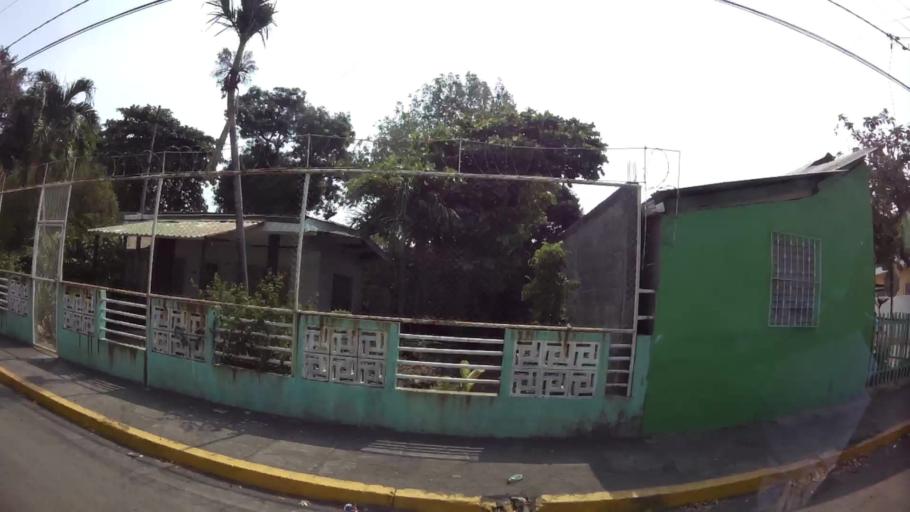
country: NI
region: Managua
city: Ciudad Sandino
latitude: 12.1302
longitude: -86.3138
